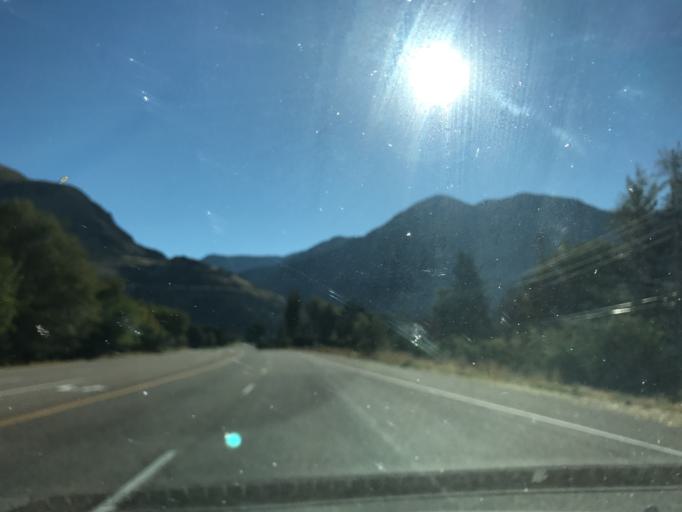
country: US
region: Utah
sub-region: Weber County
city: Ogden
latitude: 41.2406
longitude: -111.9418
